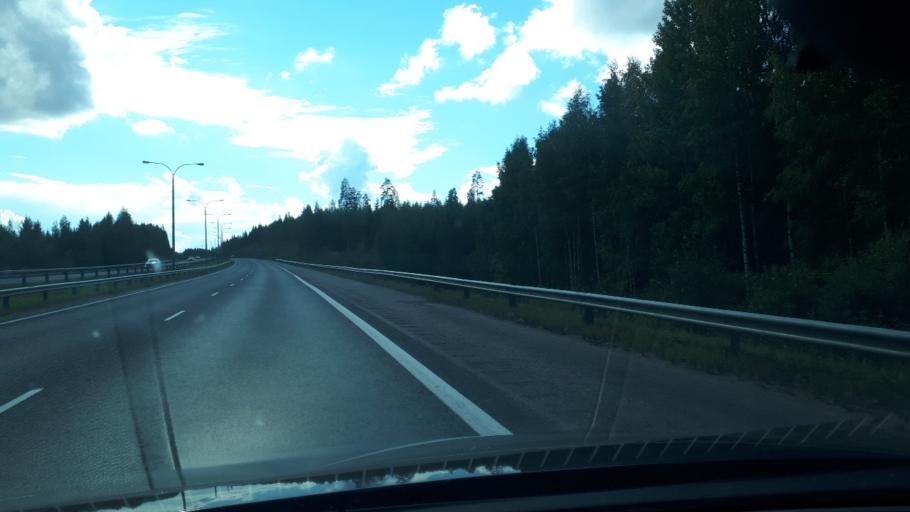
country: FI
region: Northern Savo
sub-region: Kuopio
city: Siilinjaervi
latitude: 63.0313
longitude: 27.6565
